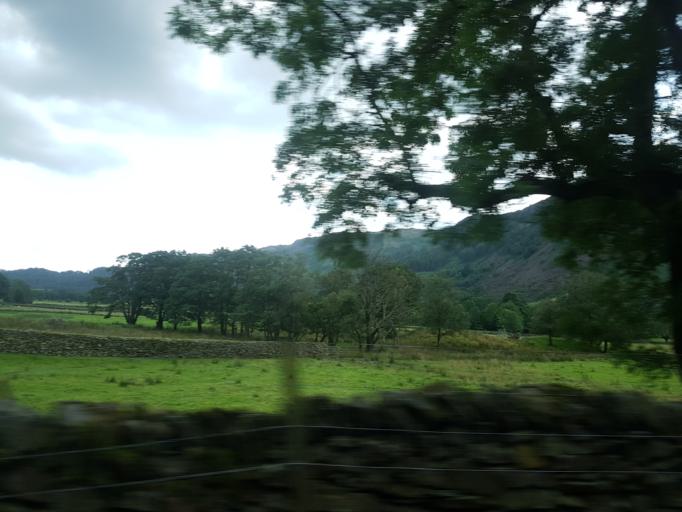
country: GB
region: England
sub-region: Cumbria
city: Ambleside
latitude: 54.4487
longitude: -3.0679
